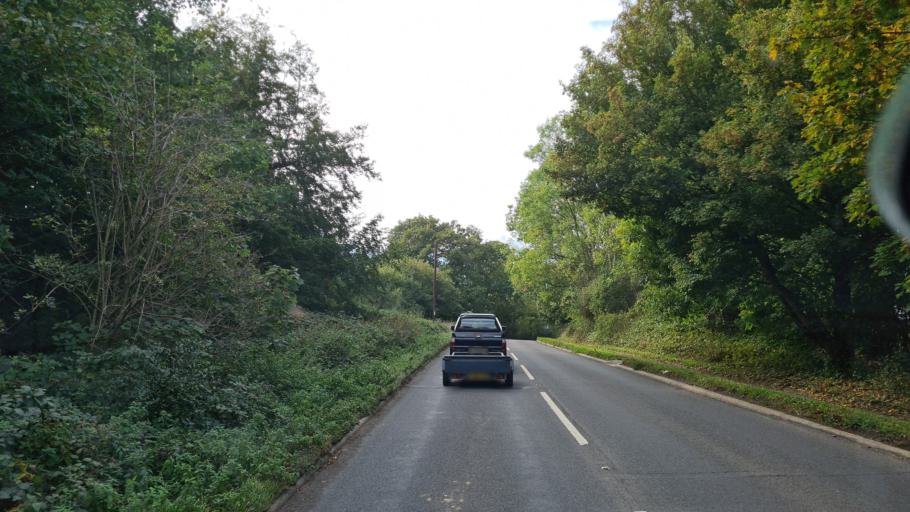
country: GB
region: England
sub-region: East Sussex
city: Bodle Street
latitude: 50.8858
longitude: 0.3106
